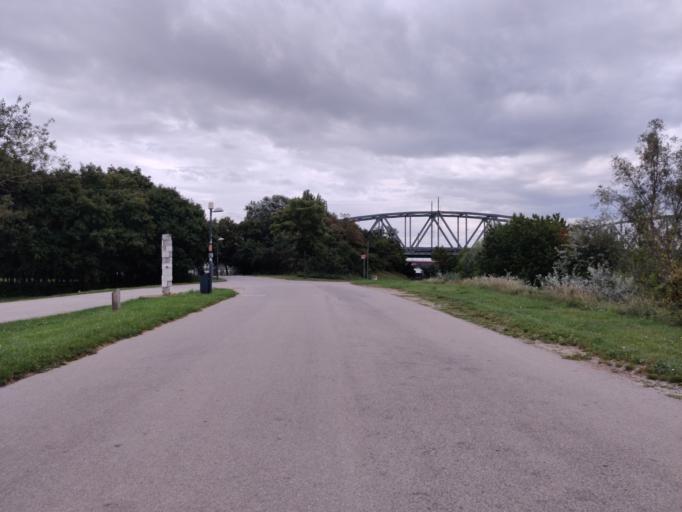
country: AT
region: Vienna
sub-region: Wien Stadt
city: Vienna
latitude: 48.2453
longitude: 16.3889
